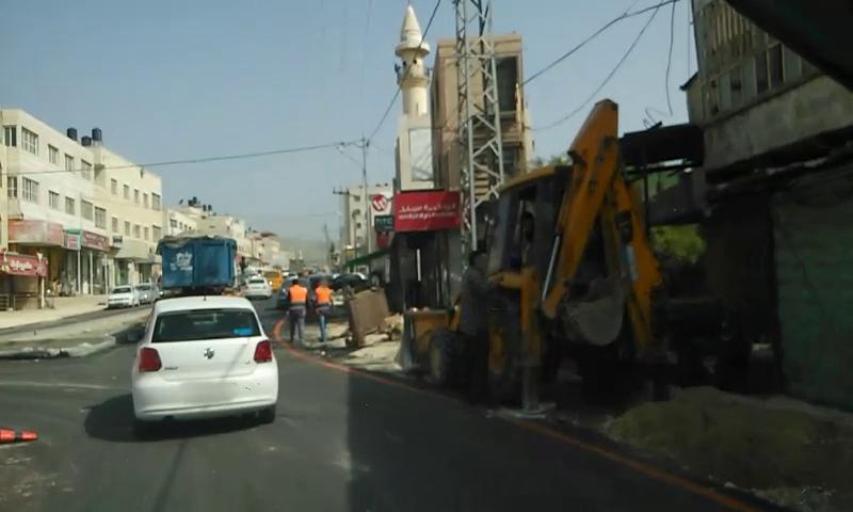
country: PS
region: West Bank
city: Huwwarah
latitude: 32.1489
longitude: 35.2580
